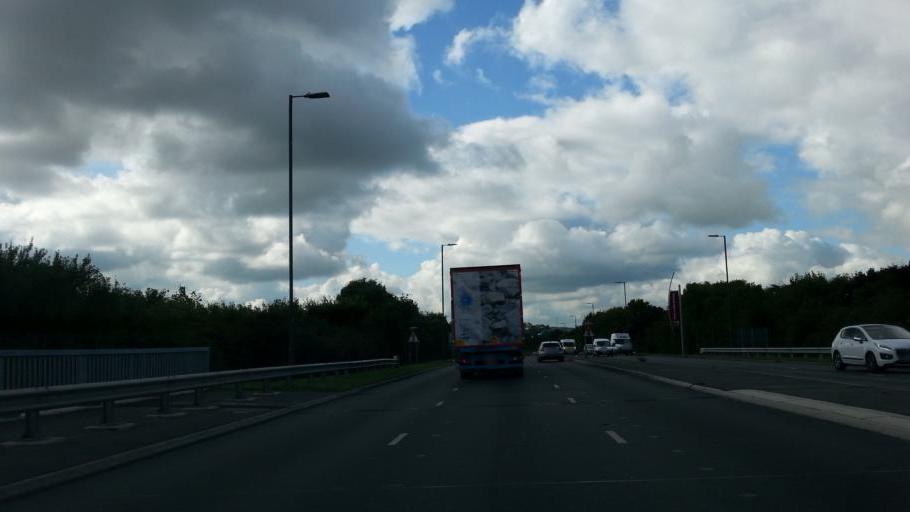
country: GB
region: England
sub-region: Slough
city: Slough
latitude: 51.5063
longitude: -0.6136
